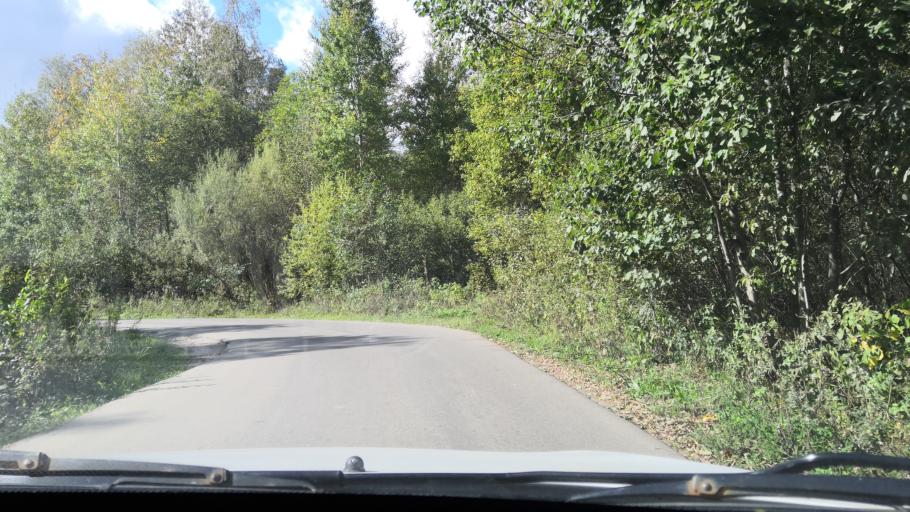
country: RU
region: Moskovskaya
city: Povarovo
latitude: 56.0650
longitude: 37.0357
